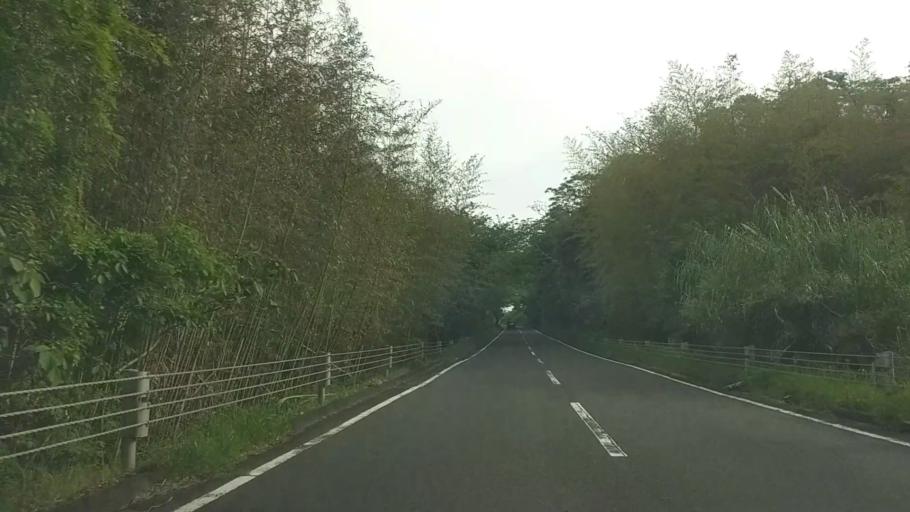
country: JP
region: Shizuoka
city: Kosai-shi
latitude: 34.7433
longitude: 137.5981
